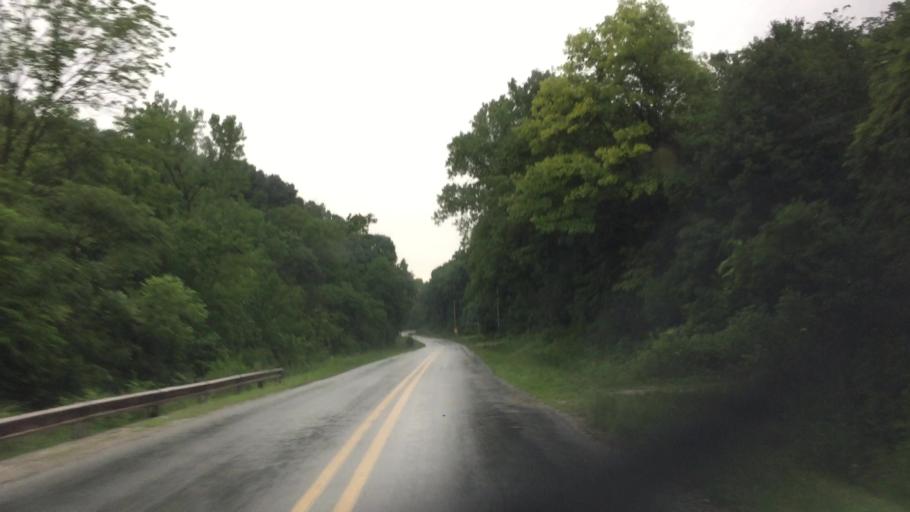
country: US
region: Iowa
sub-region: Lee County
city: Fort Madison
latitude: 40.6080
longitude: -91.2796
